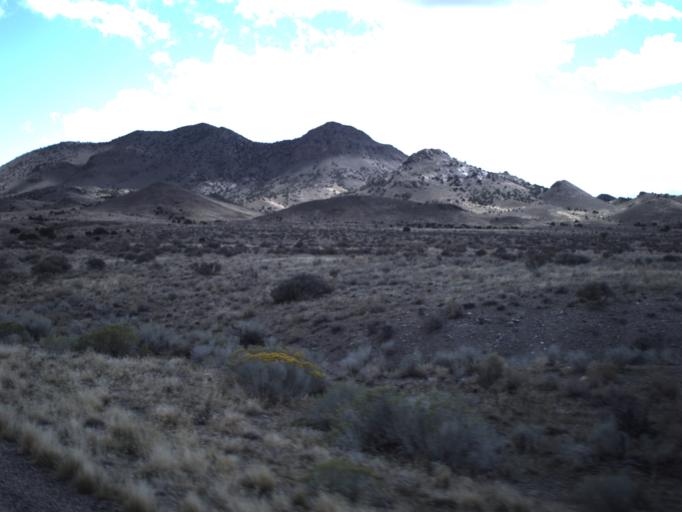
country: US
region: Utah
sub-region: Beaver County
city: Milford
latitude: 38.4357
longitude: -113.3004
